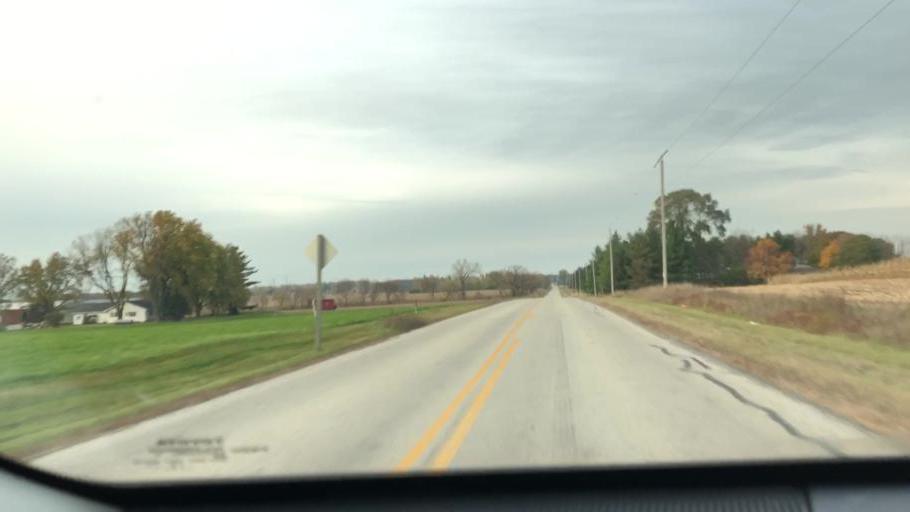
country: US
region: Wisconsin
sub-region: Outagamie County
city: Seymour
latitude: 44.4473
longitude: -88.3505
